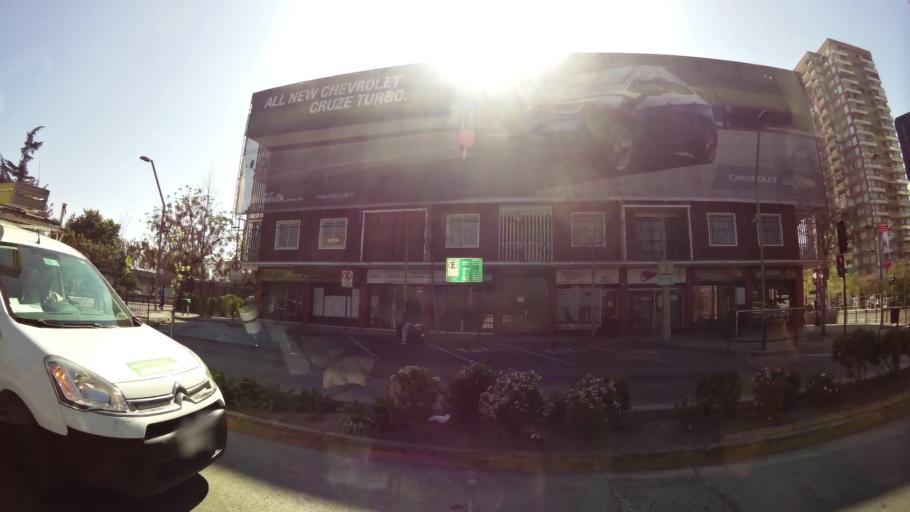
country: CL
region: Santiago Metropolitan
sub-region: Provincia de Santiago
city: Villa Presidente Frei, Nunoa, Santiago, Chile
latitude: -33.4134
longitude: -70.5835
